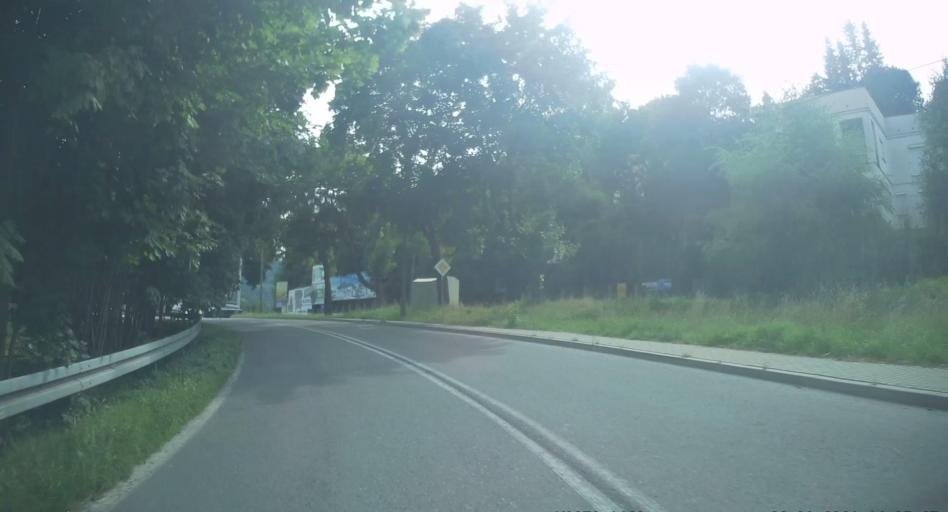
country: PL
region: Lesser Poland Voivodeship
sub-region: Powiat myslenicki
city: Myslenice
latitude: 49.8258
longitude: 19.9416
